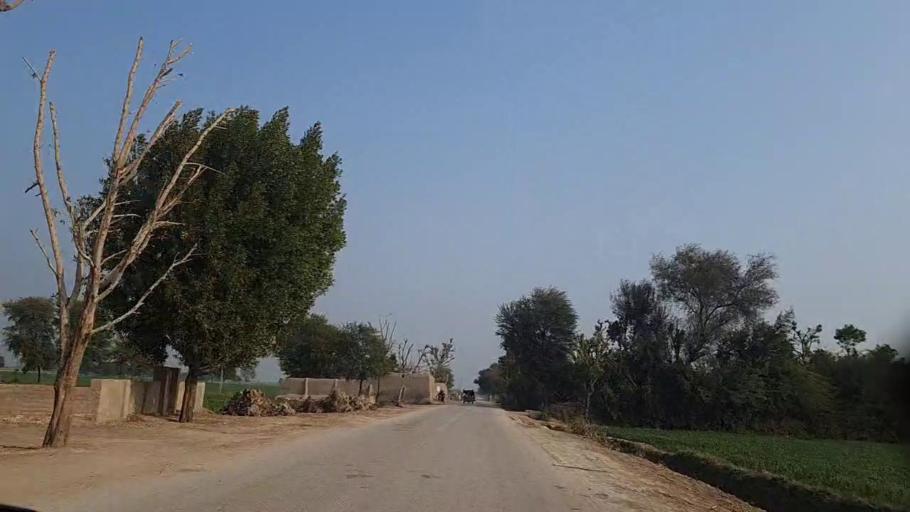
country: PK
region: Sindh
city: Sann
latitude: 26.1430
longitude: 68.1502
